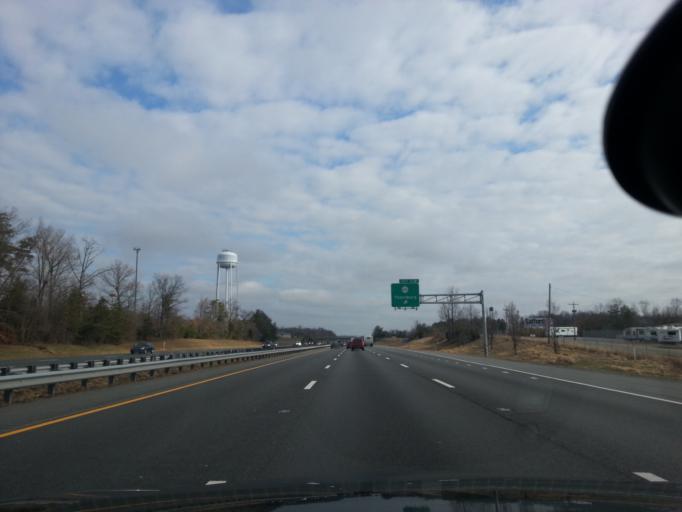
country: US
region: Virginia
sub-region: Spotsylvania County
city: Spotsylvania Courthouse
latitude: 38.1268
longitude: -77.5138
